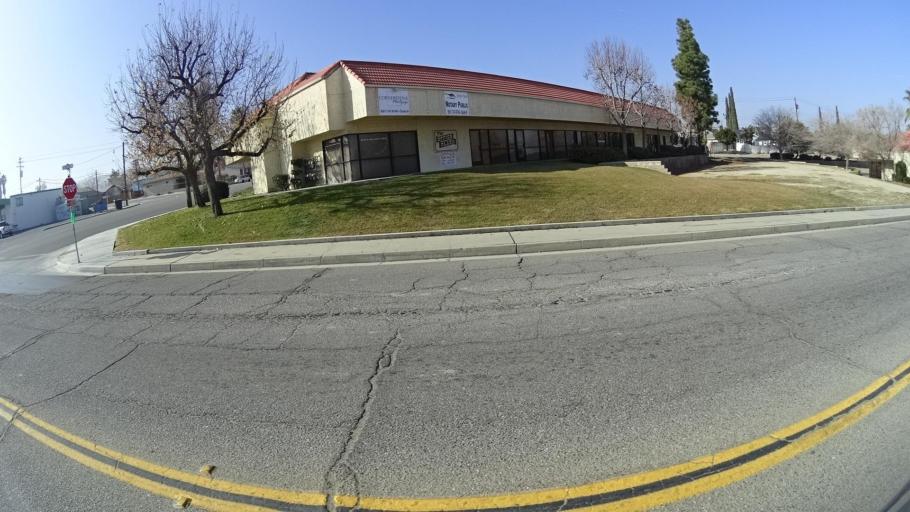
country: US
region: California
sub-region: Kern County
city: Taft Heights
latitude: 35.1370
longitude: -119.4652
